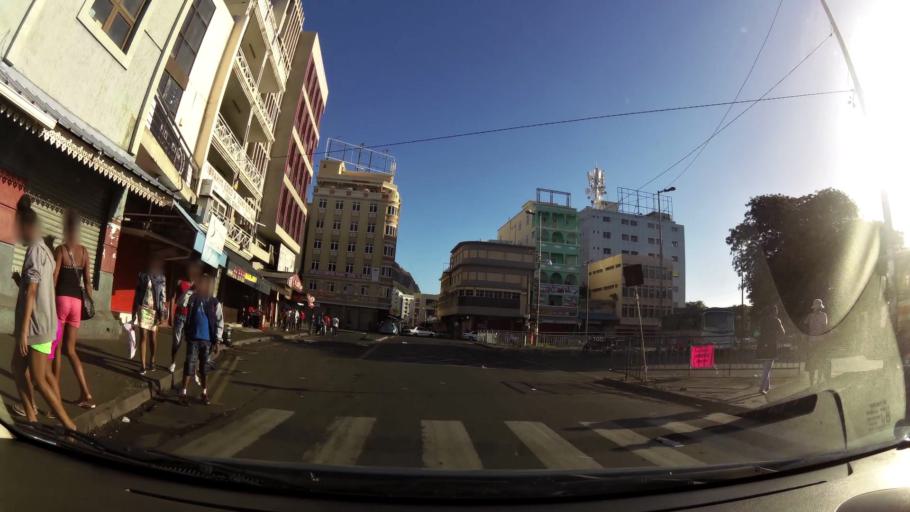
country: MU
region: Port Louis
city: Port Louis
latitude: -20.1593
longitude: 57.5040
